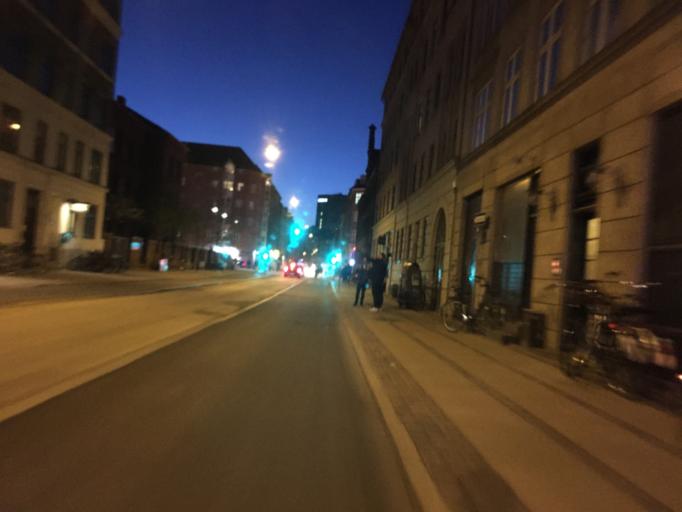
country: DK
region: Capital Region
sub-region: Kobenhavn
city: Copenhagen
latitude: 55.6698
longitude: 12.5583
